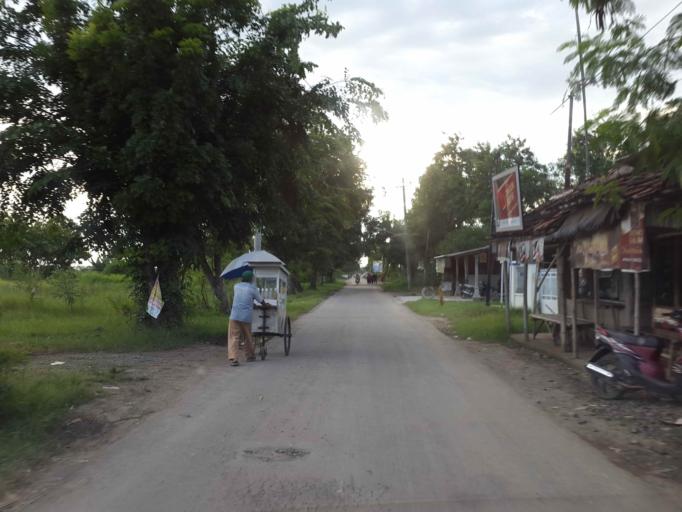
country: ID
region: Central Java
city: Ketanggungan
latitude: -6.9043
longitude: 108.8883
